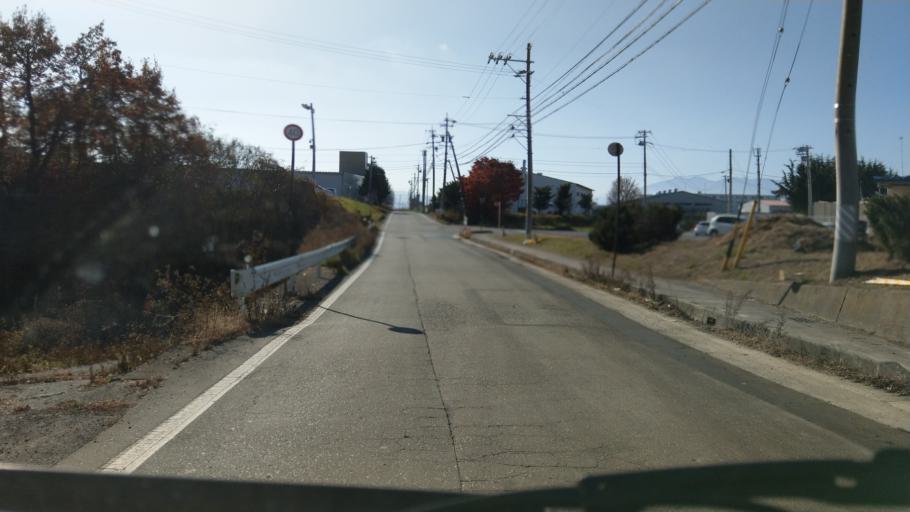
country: JP
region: Nagano
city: Komoro
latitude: 36.2930
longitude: 138.4860
